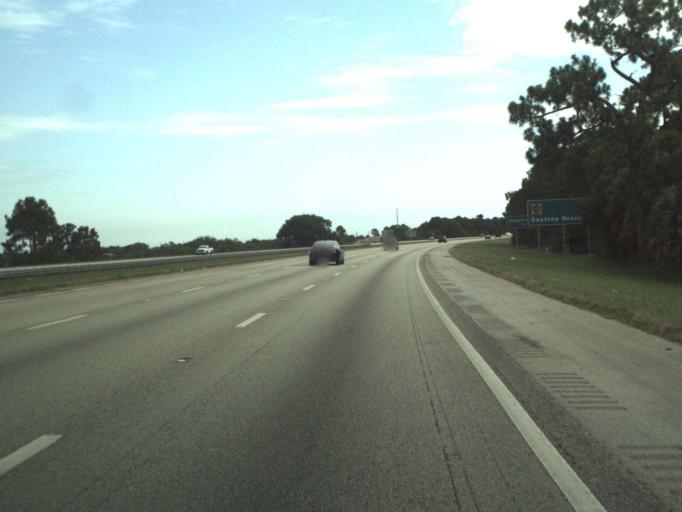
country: US
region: Florida
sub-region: Saint Lucie County
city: Port Saint Lucie
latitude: 27.2781
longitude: -80.4258
